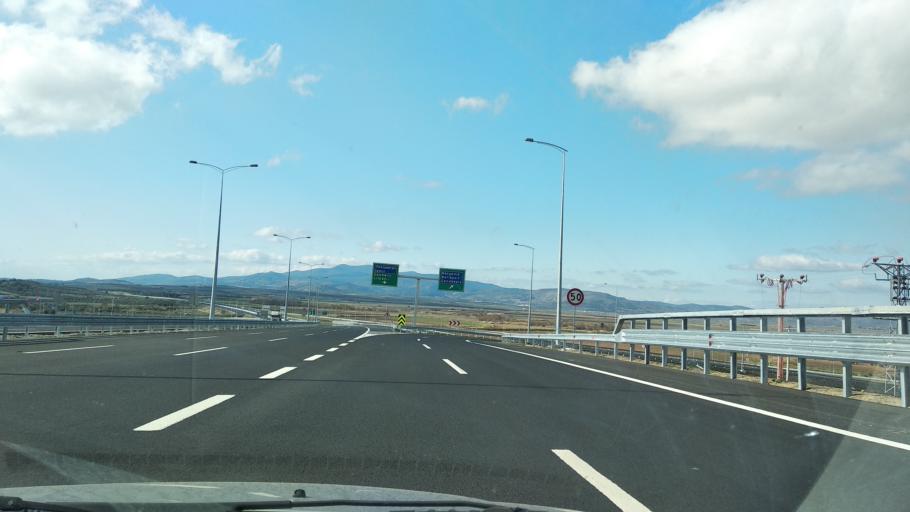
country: TR
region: Izmir
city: Zeytindag
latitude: 38.9737
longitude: 27.0500
